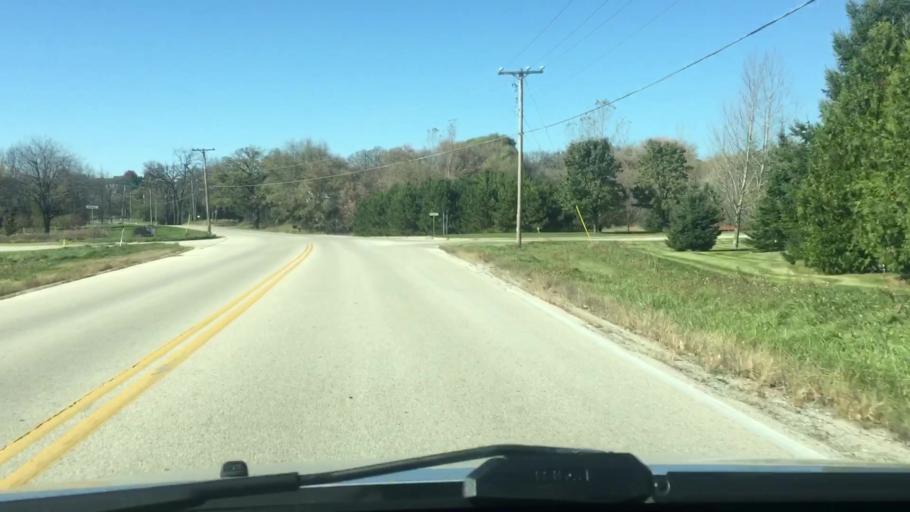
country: US
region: Wisconsin
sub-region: Waukesha County
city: Wales
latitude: 42.9912
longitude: -88.3661
